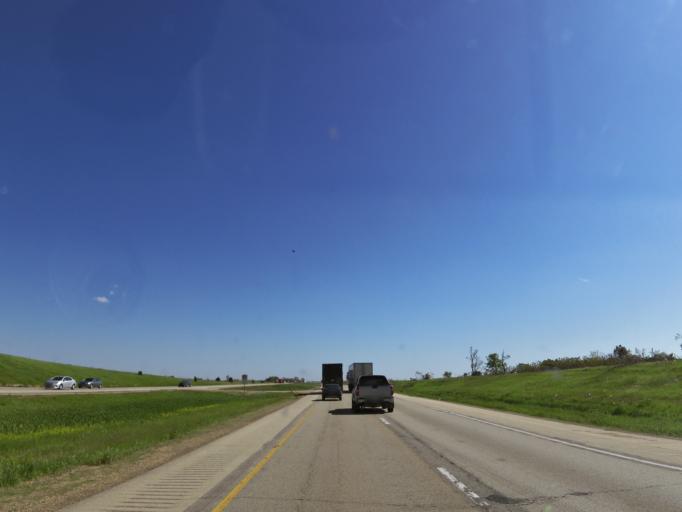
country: US
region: Illinois
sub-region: Ogle County
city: Davis Junction
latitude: 42.0417
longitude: -89.0211
